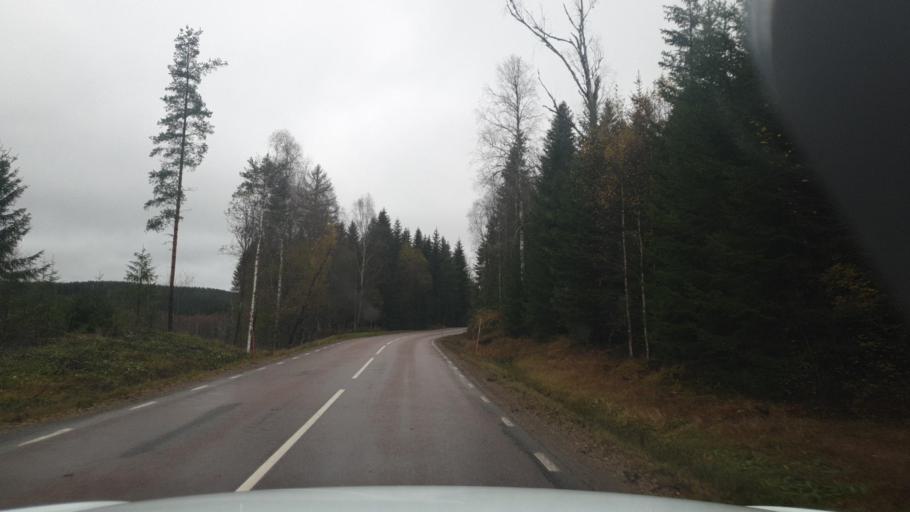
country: SE
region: Vaermland
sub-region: Eda Kommun
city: Charlottenberg
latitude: 59.8077
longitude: 12.1547
